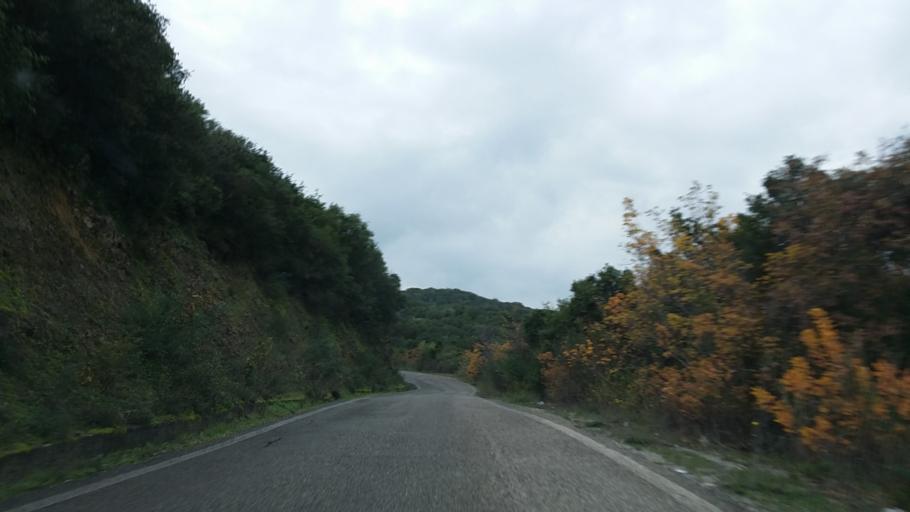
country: GR
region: West Greece
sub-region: Nomos Aitolias kai Akarnanias
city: Fitiai
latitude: 38.7204
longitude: 21.1866
